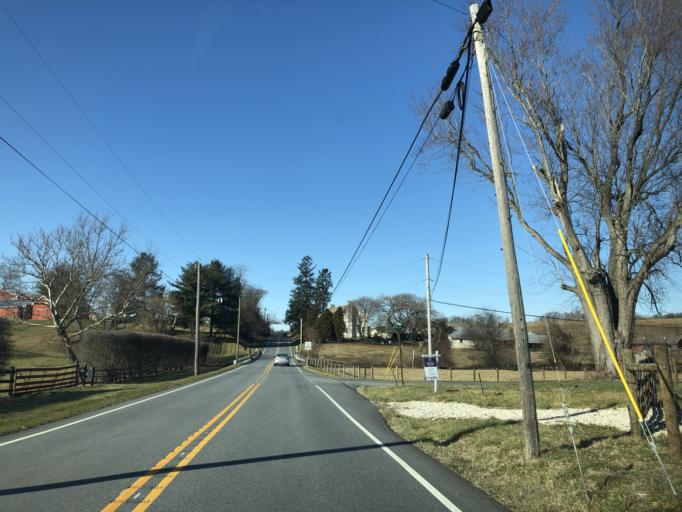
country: US
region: Pennsylvania
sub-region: Chester County
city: Upland
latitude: 39.9070
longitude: -75.7987
